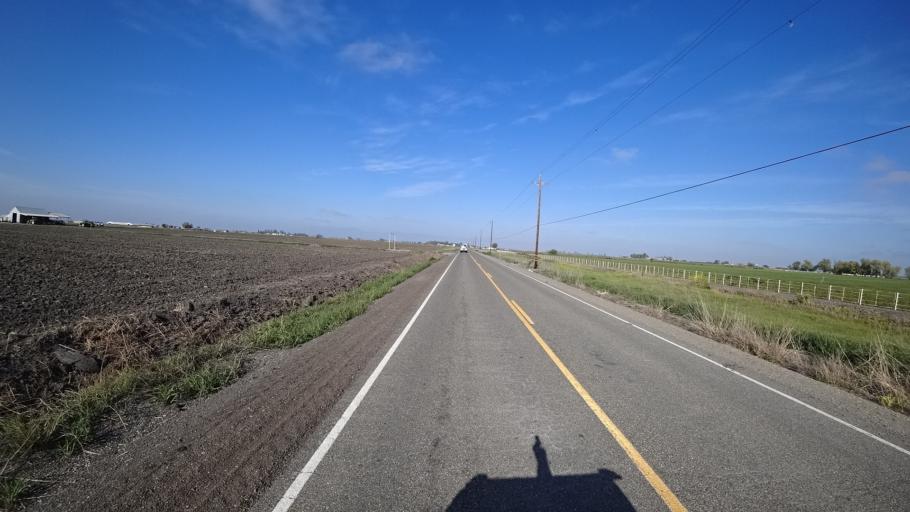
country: US
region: California
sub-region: Glenn County
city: Willows
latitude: 39.5827
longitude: -122.0749
